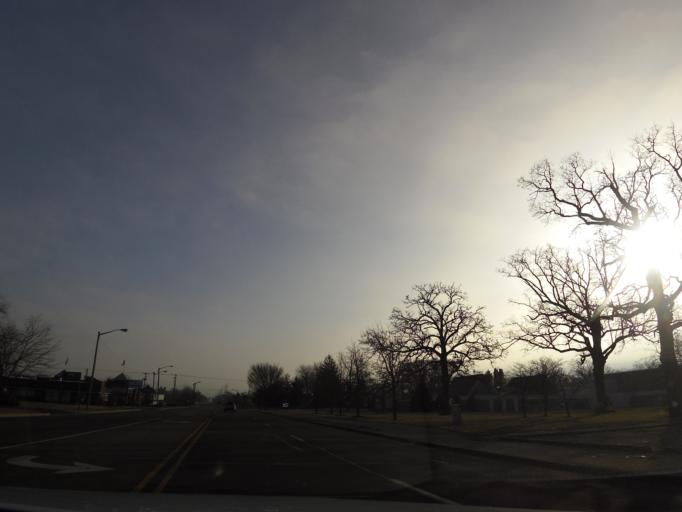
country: US
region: Indiana
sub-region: Bartholomew County
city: Columbus
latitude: 39.2230
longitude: -85.8971
